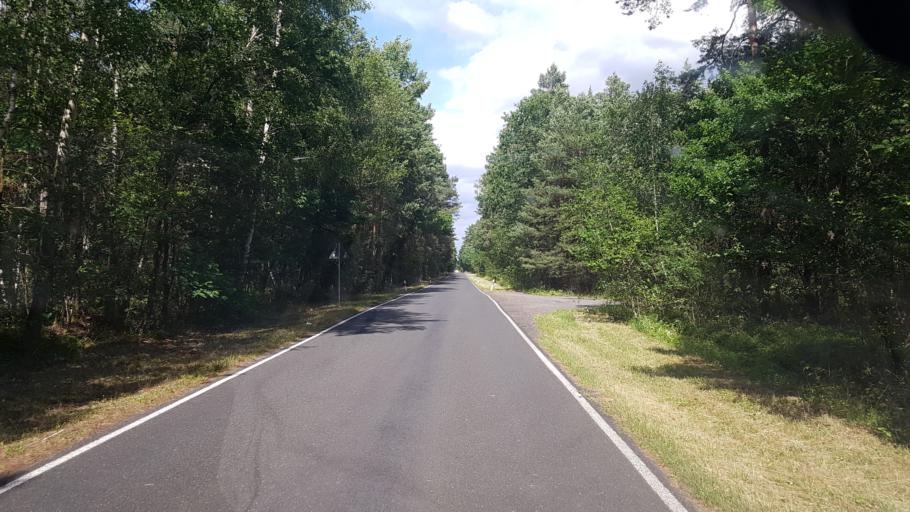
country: DE
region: Brandenburg
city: Sallgast
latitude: 51.5819
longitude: 13.9180
